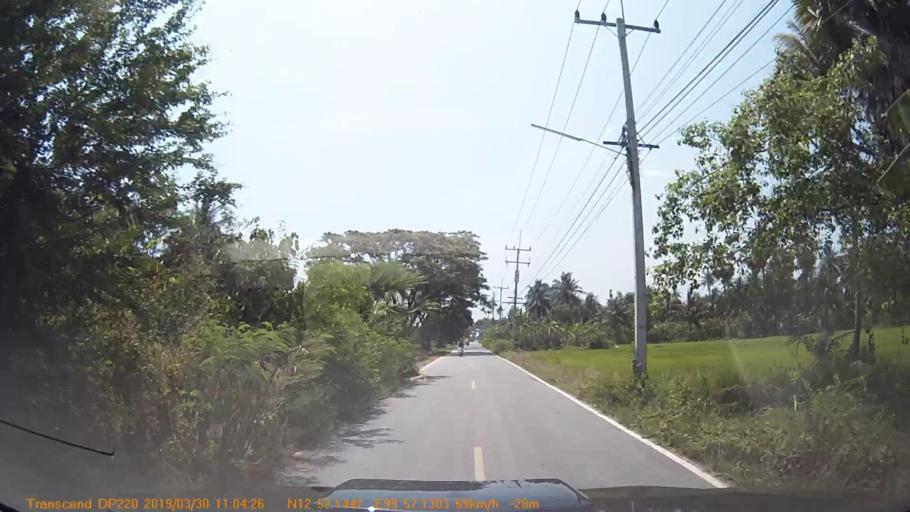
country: TH
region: Phetchaburi
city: Cha-am
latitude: 12.8690
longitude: 99.9522
